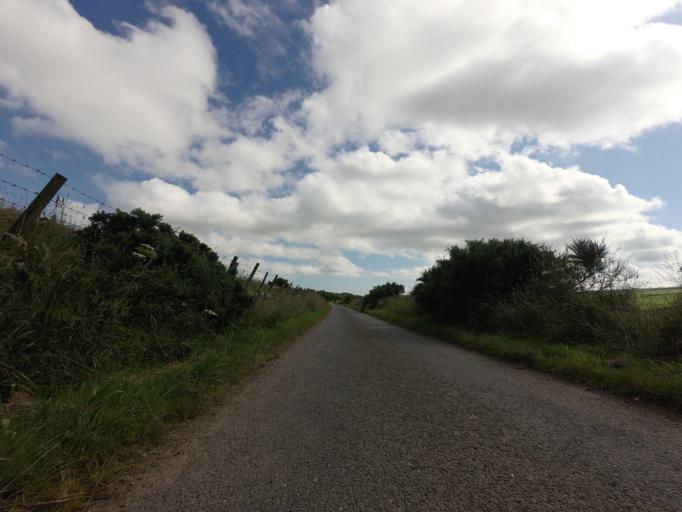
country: GB
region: Scotland
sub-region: Aberdeenshire
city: Banff
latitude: 57.6034
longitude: -2.5127
